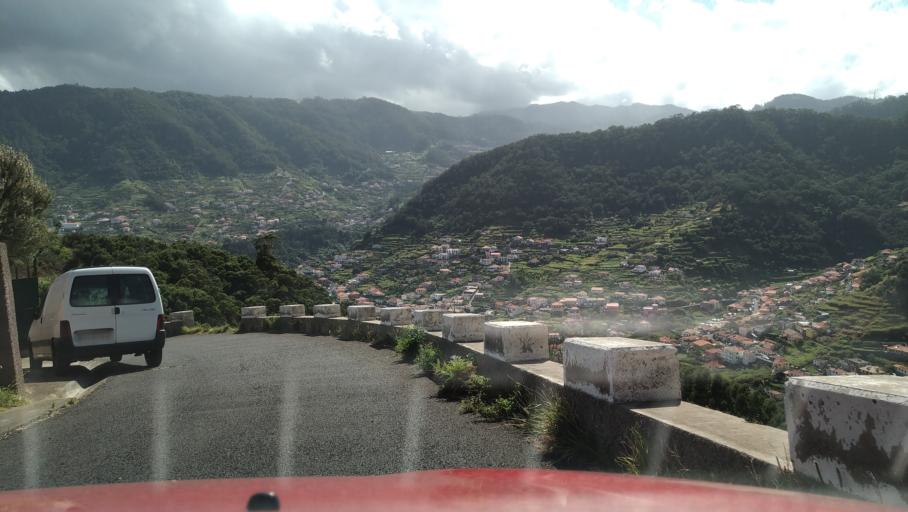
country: PT
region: Madeira
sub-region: Machico
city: Canical
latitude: 32.7402
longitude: -16.7714
